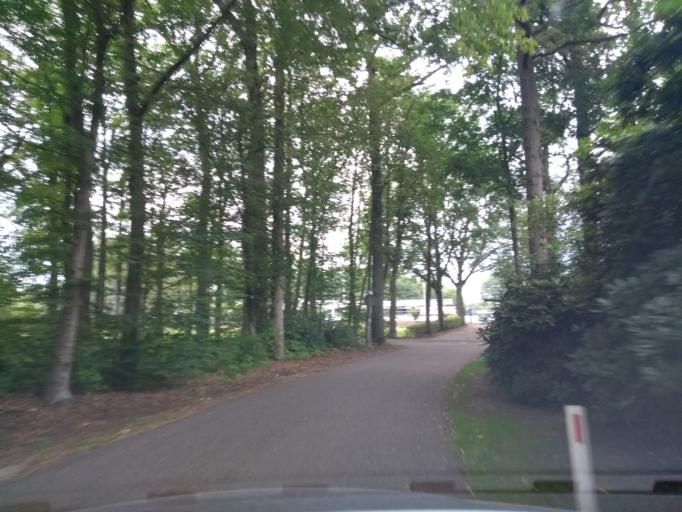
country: NL
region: Overijssel
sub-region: Gemeente Oldenzaal
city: Oldenzaal
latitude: 52.3737
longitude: 6.9959
